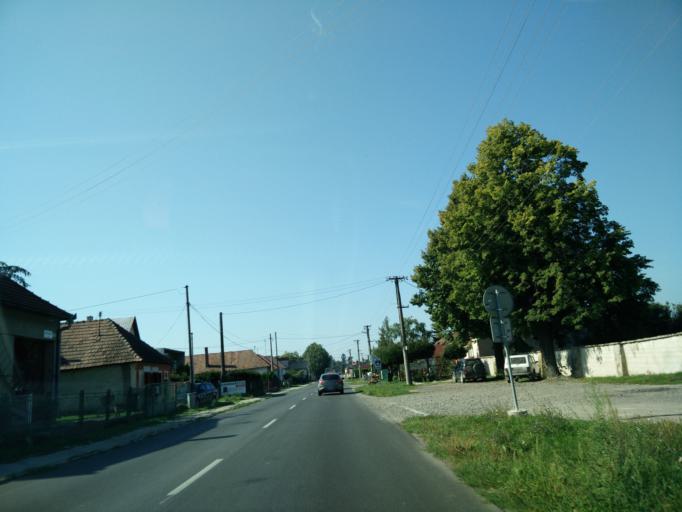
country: SK
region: Nitriansky
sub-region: Okres Nitra
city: Nitra
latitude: 48.4988
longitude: 18.1620
